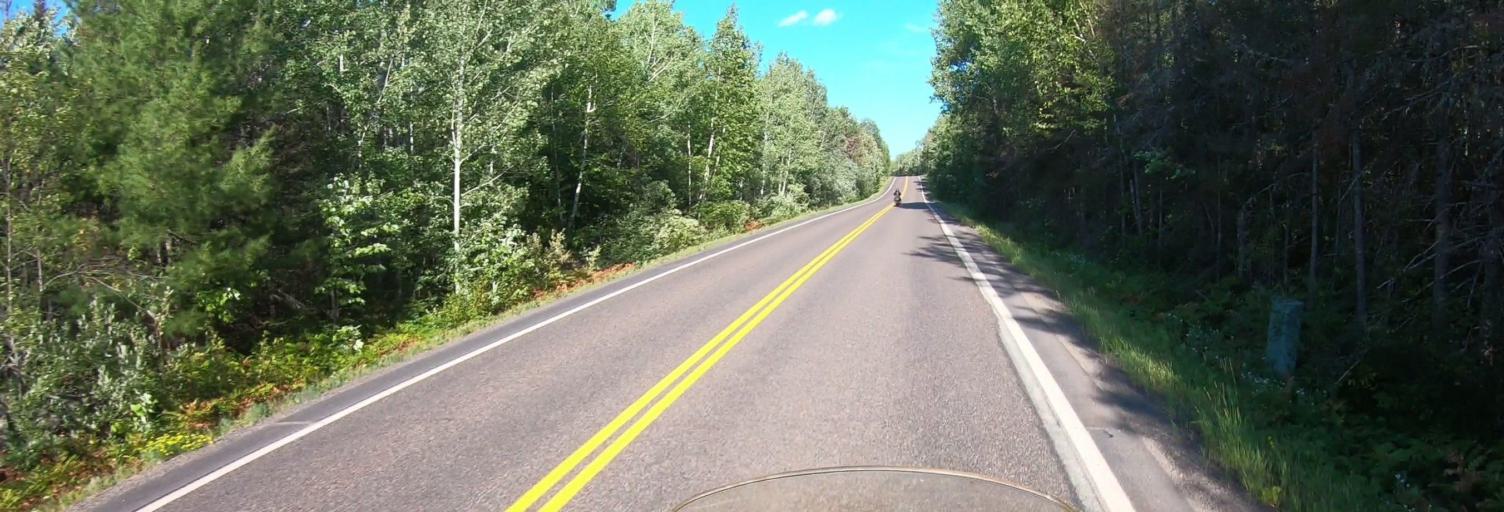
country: US
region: Minnesota
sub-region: Saint Louis County
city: Ely
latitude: 47.9597
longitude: -91.5860
